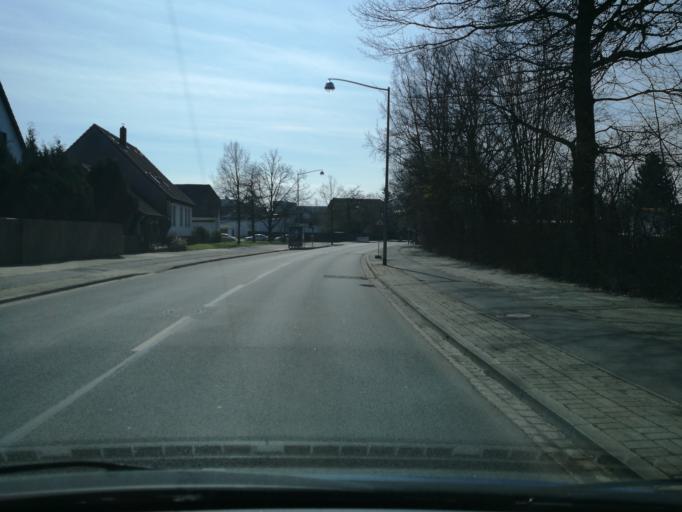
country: DE
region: Lower Saxony
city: Ronnenberg
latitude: 52.3684
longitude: 9.6707
